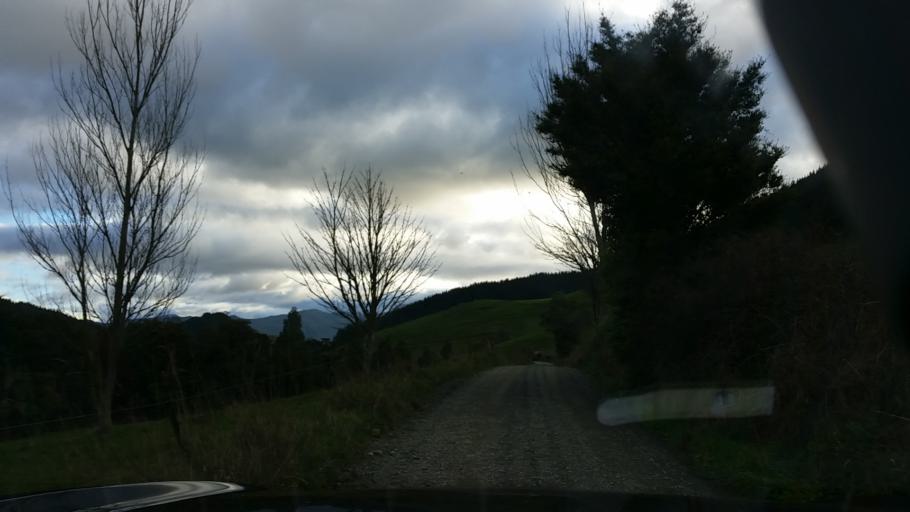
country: NZ
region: Nelson
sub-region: Nelson City
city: Nelson
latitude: -41.2081
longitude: 173.6395
